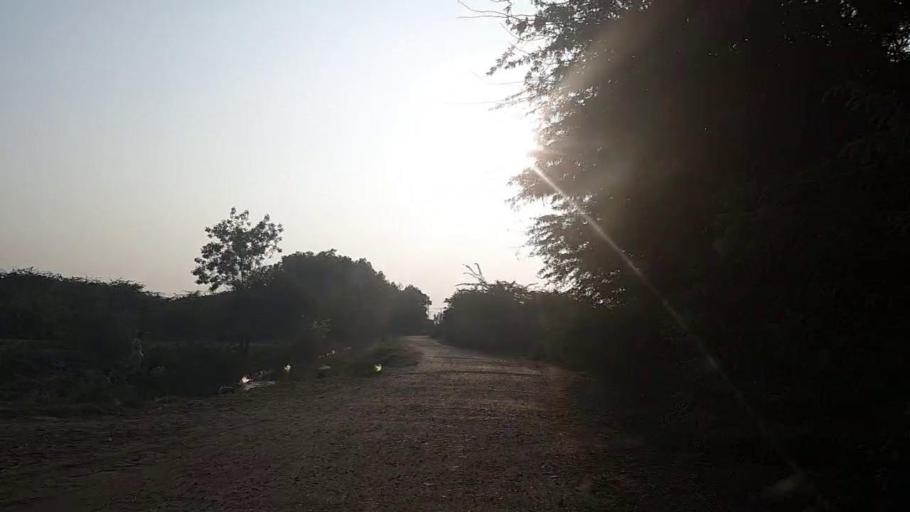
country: PK
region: Sindh
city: Mirpur Sakro
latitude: 24.5669
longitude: 67.6239
